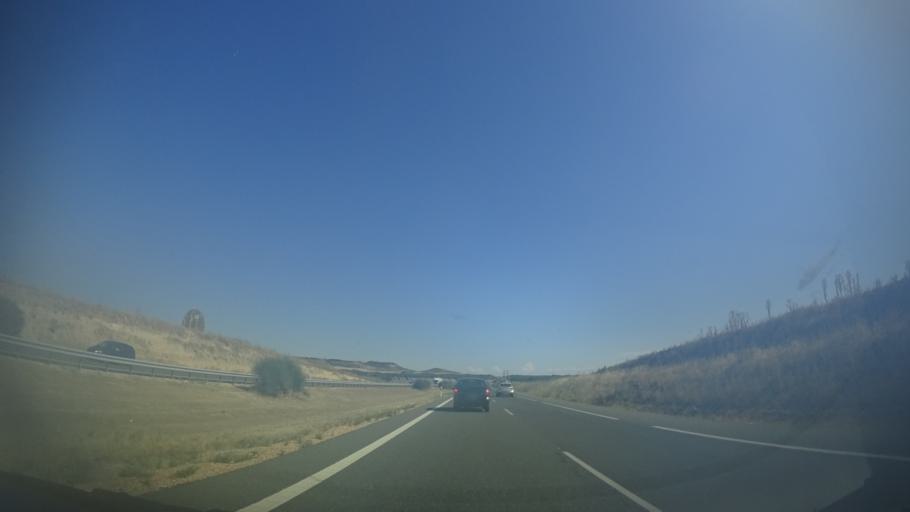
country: ES
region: Castille and Leon
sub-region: Provincia de Valladolid
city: Bercero
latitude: 41.5573
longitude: -5.0819
